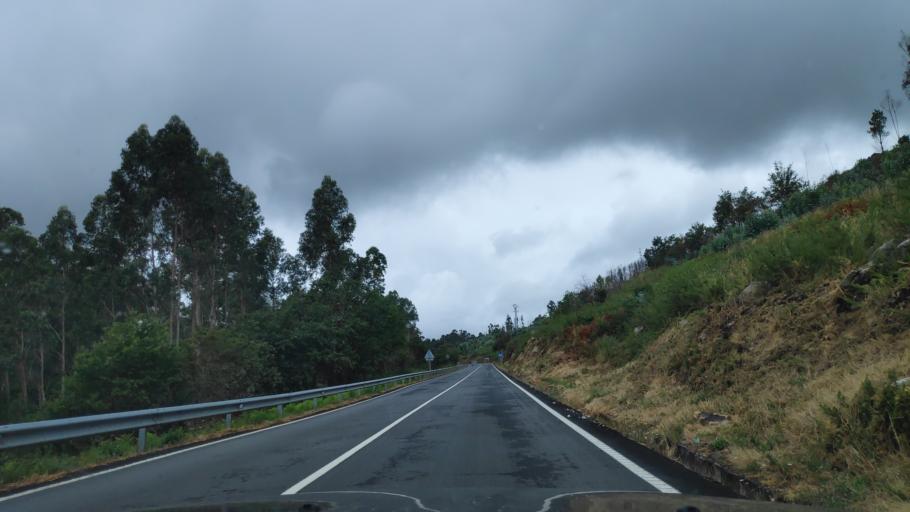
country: ES
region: Galicia
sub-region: Provincia de Pontevedra
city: Catoira
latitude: 42.6954
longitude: -8.7459
